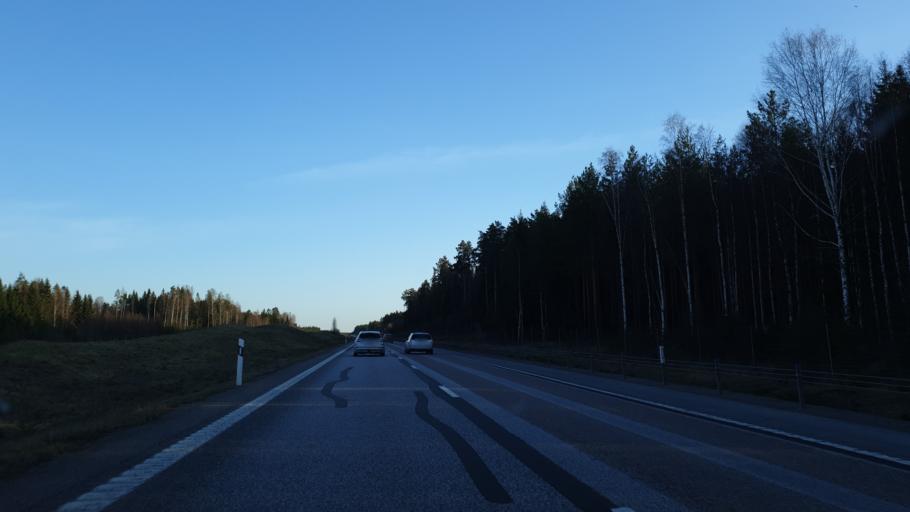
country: SE
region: Uppsala
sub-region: Tierps Kommun
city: Tierp
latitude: 60.2602
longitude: 17.4999
